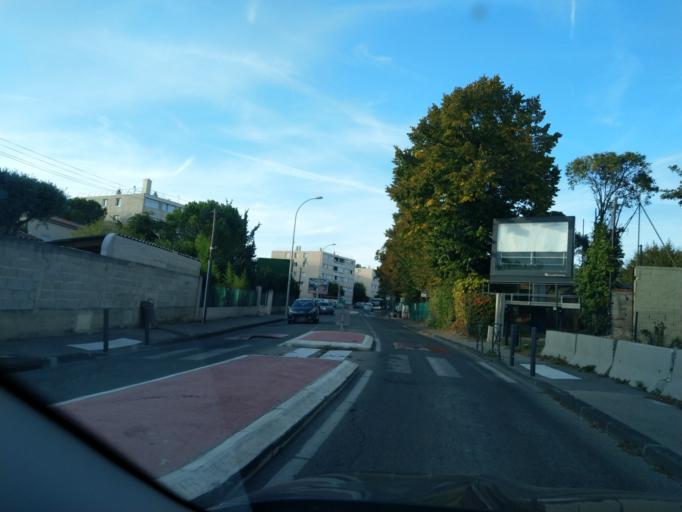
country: FR
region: Provence-Alpes-Cote d'Azur
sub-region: Departement des Bouches-du-Rhone
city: Marseille 12
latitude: 43.2990
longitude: 5.4506
